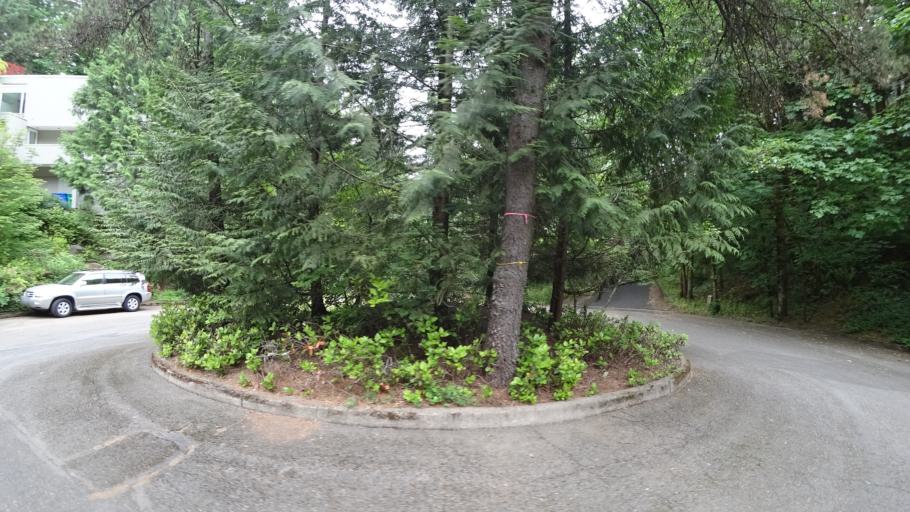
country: US
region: Oregon
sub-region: Multnomah County
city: Portland
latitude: 45.5001
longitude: -122.7022
